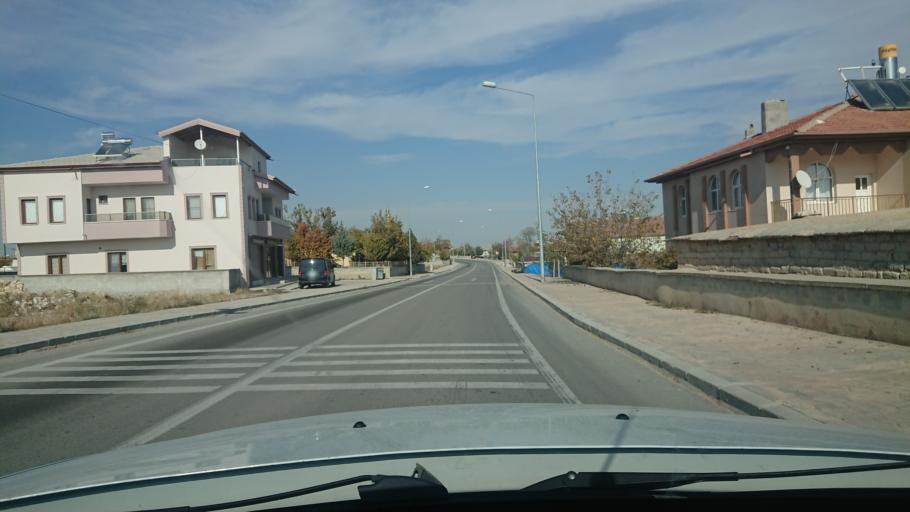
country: TR
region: Aksaray
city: Sultanhani
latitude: 38.2498
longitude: 33.4491
